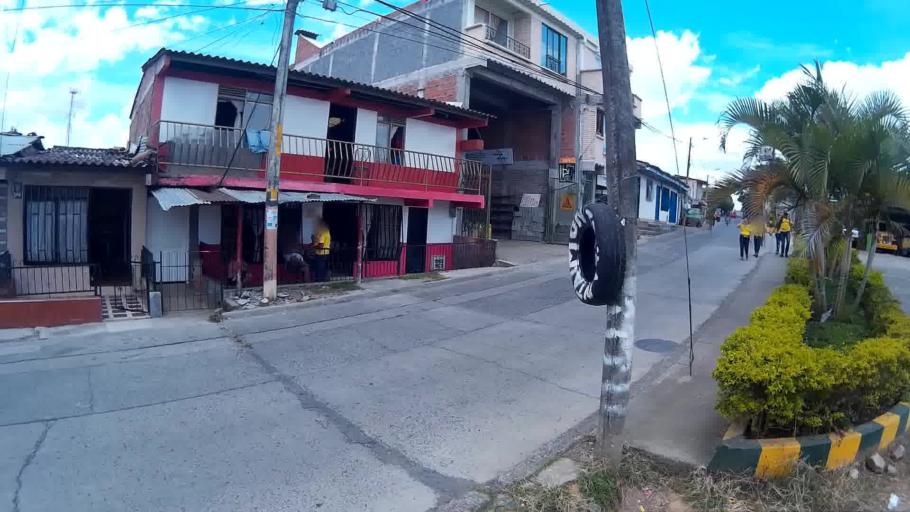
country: CO
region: Valle del Cauca
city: Ulloa
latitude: 4.7367
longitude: -75.7134
